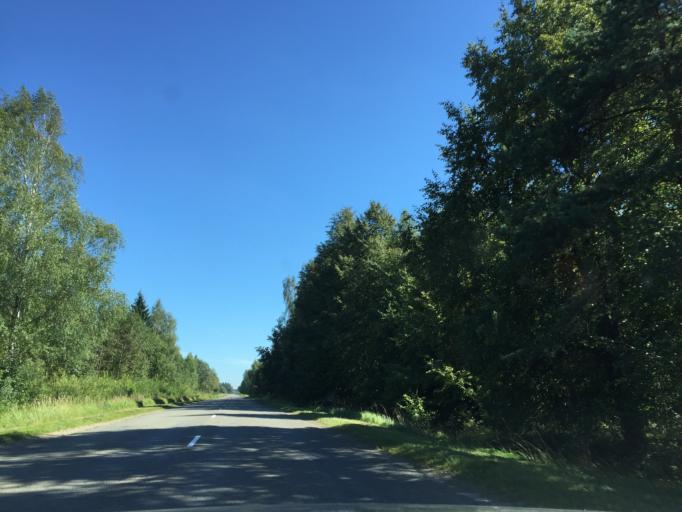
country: LV
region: Akniste
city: Akniste
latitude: 56.1516
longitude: 25.7754
